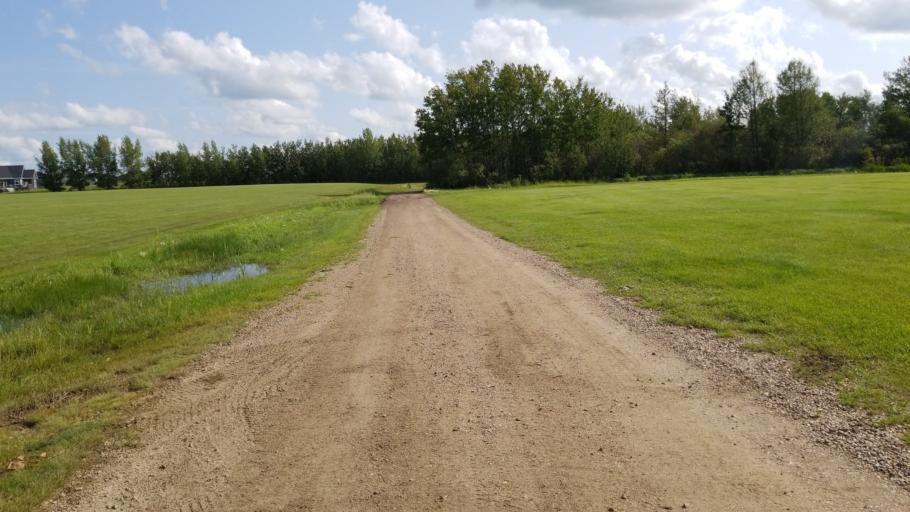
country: CA
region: Saskatchewan
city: Lloydminster
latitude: 53.2580
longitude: -110.0440
